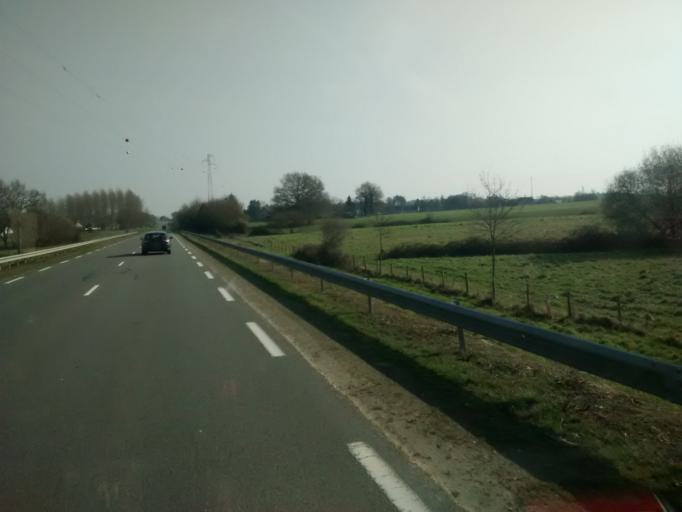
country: FR
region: Brittany
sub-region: Departement d'Ille-et-Vilaine
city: Chavagne
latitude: 48.0746
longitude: -1.7906
